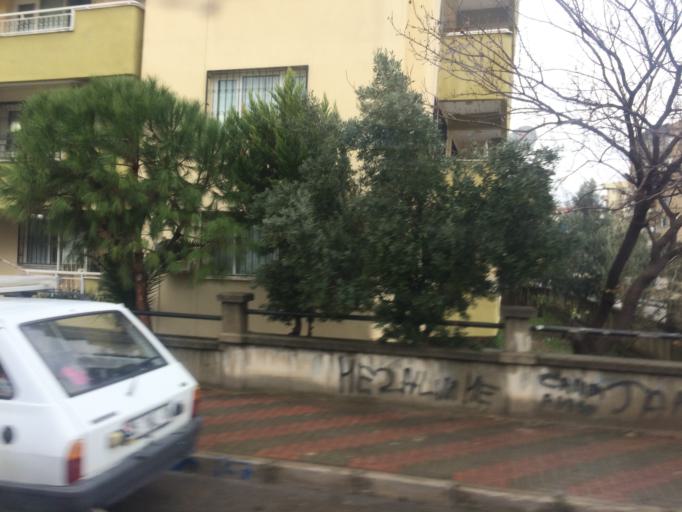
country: TR
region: Izmir
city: Karsiyaka
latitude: 38.4914
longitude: 27.0567
